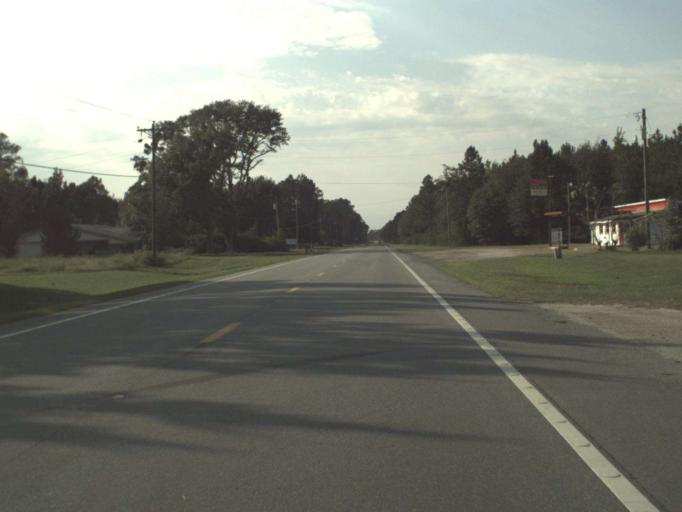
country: US
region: Florida
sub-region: Gulf County
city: Wewahitchka
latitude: 30.1267
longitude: -85.2246
